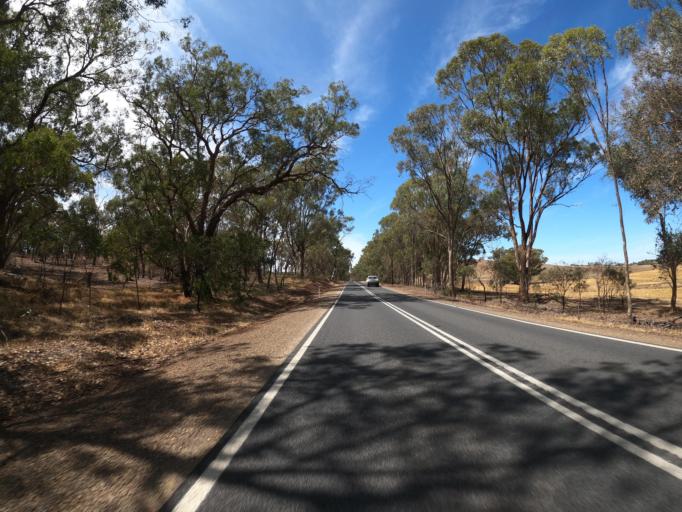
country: AU
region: Victoria
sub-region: Benalla
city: Benalla
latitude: -36.3768
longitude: 145.9752
